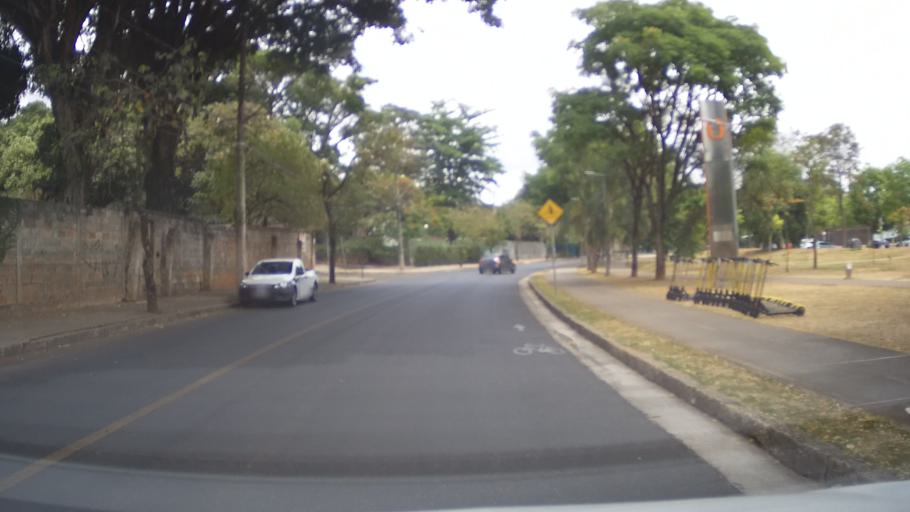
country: BR
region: Minas Gerais
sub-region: Belo Horizonte
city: Belo Horizonte
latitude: -19.8519
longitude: -43.9924
